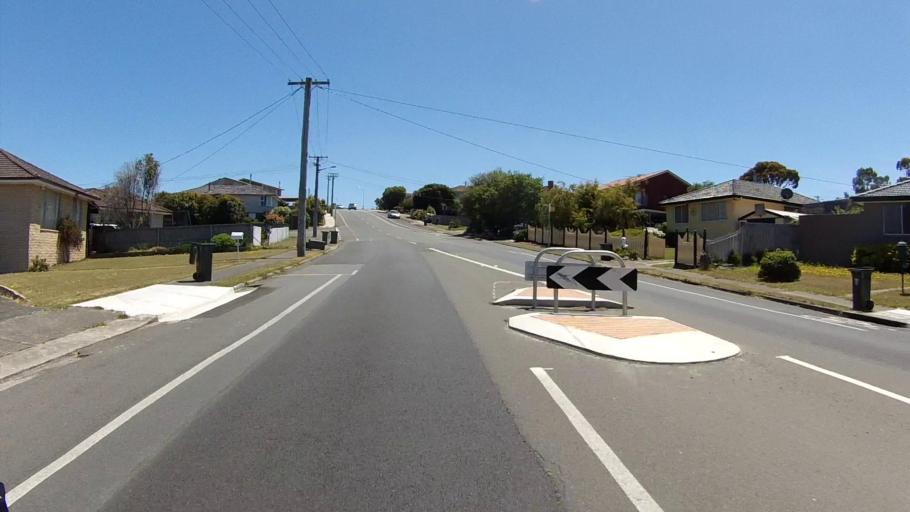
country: AU
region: Tasmania
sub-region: Clarence
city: Rokeby
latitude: -42.8923
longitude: 147.4313
